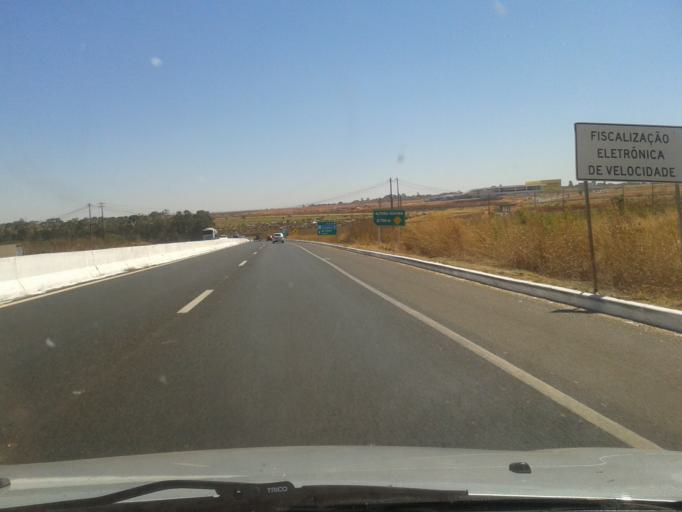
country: BR
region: Minas Gerais
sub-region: Uberlandia
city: Uberlandia
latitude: -18.9175
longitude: -48.2227
